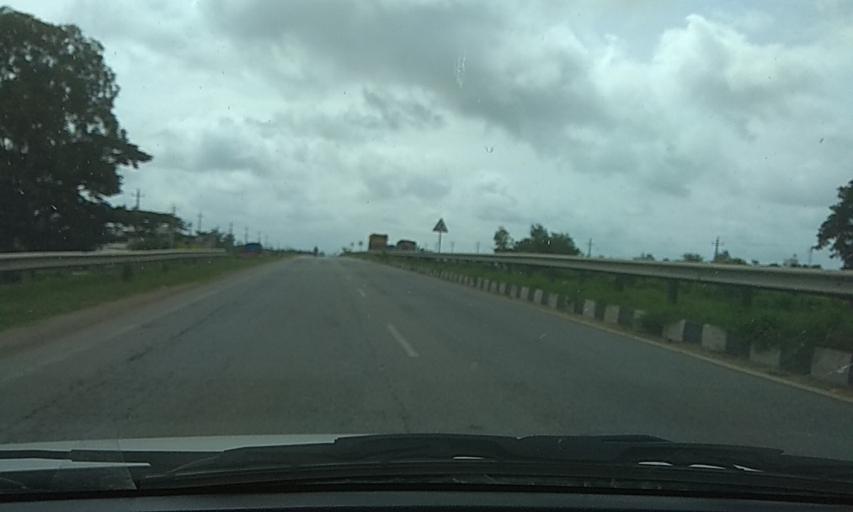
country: IN
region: Karnataka
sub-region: Davanagere
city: Harihar
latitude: 14.4554
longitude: 75.8672
